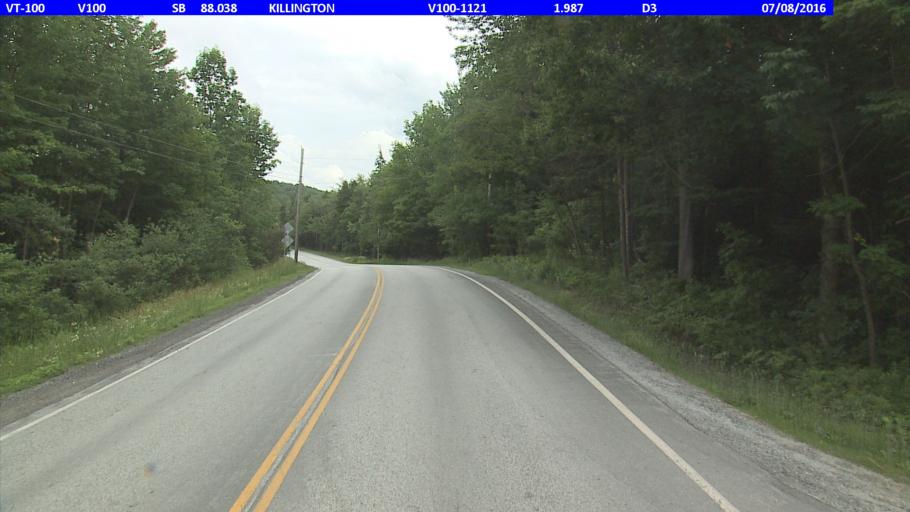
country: US
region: Vermont
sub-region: Rutland County
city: Rutland
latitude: 43.6938
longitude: -72.8143
